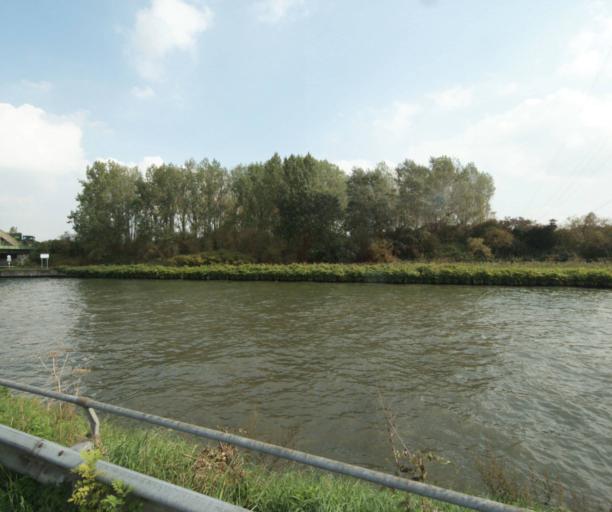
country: FR
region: Nord-Pas-de-Calais
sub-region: Departement du Nord
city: Santes
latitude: 50.5689
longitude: 2.9651
